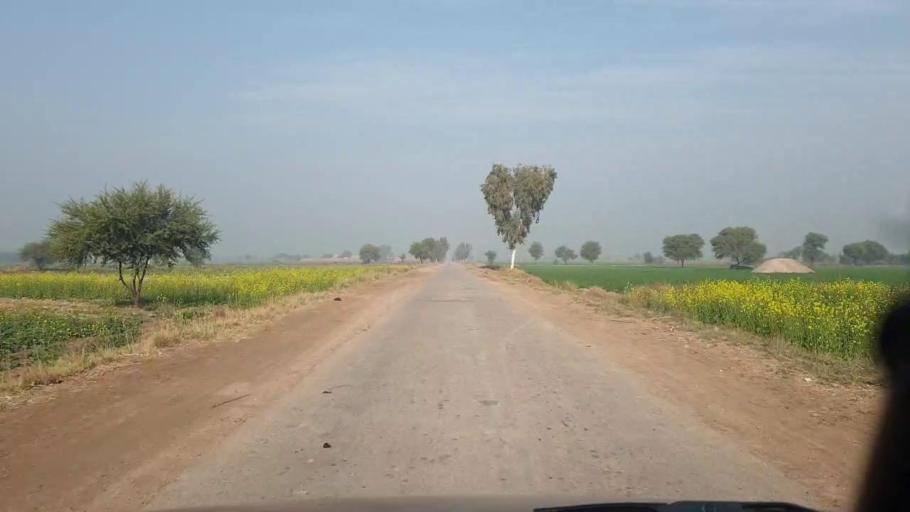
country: PK
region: Sindh
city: Shahdadpur
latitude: 25.9754
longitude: 68.5756
